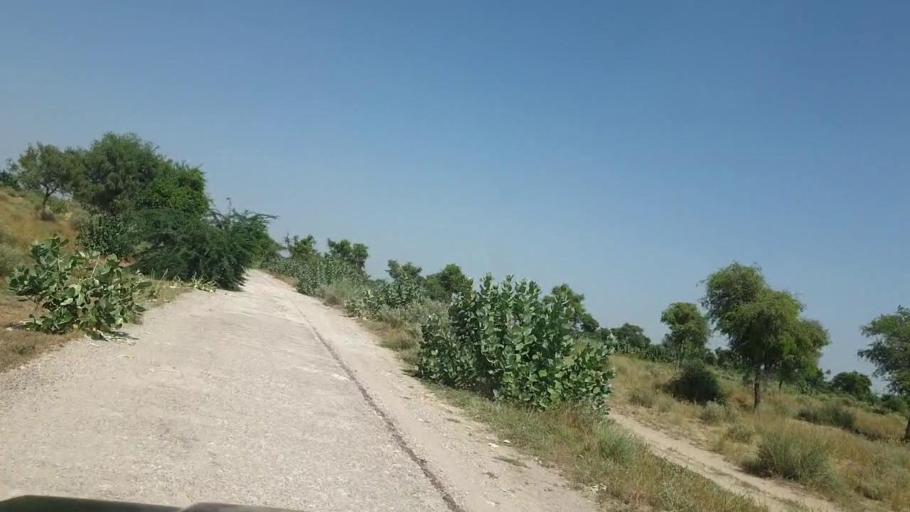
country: PK
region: Sindh
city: Chor
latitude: 25.3899
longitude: 70.3132
